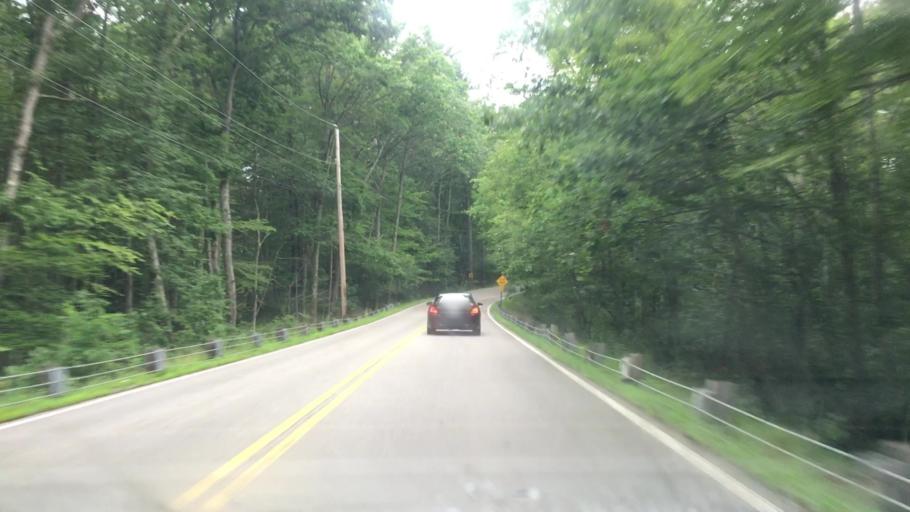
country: US
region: New Hampshire
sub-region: Rockingham County
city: Greenland
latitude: 43.0947
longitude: -70.8426
